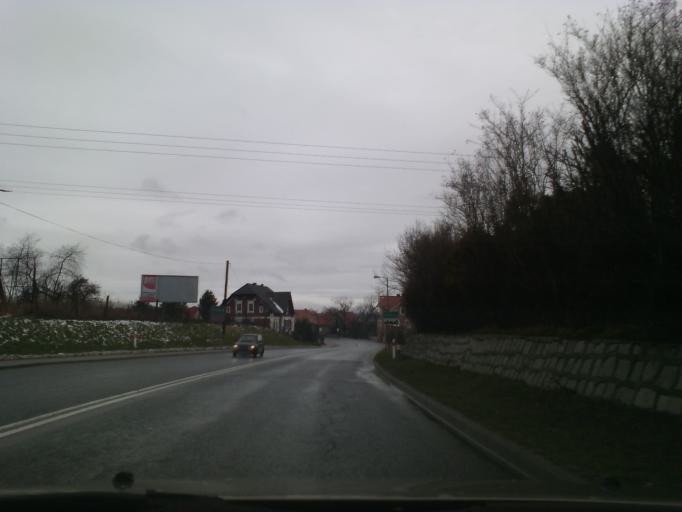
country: PL
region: Lower Silesian Voivodeship
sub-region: Powiat swidnicki
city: Swidnica
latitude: 50.8425
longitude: 16.4587
